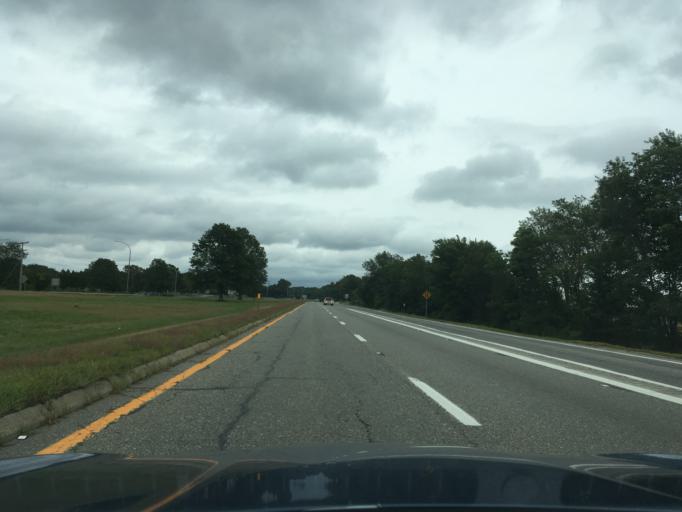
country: US
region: Massachusetts
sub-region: Bristol County
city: Seekonk
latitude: 41.7922
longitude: -71.3484
